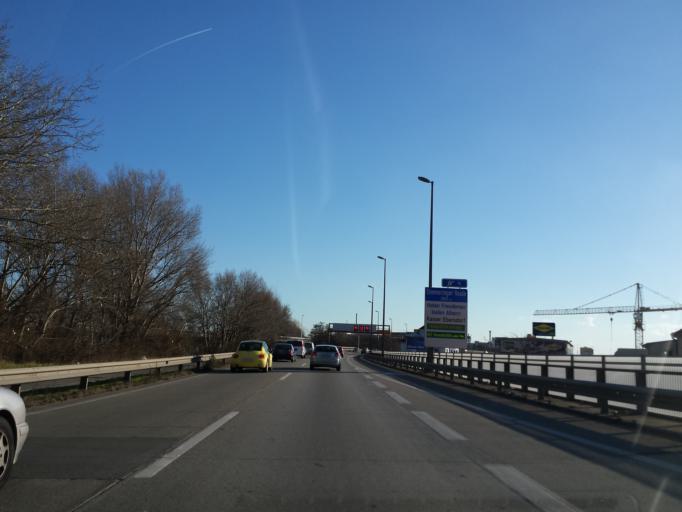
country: AT
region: Lower Austria
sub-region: Politischer Bezirk Wien-Umgebung
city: Schwechat
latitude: 48.1809
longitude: 16.4484
